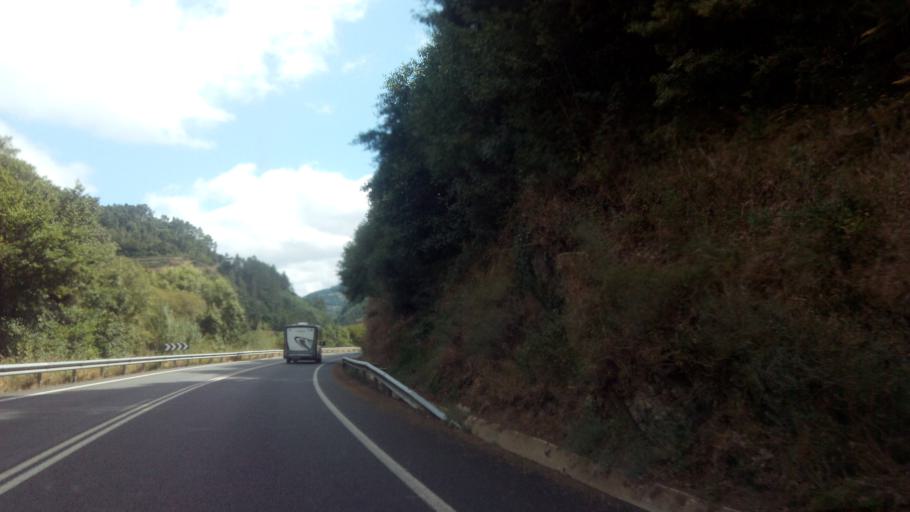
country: ES
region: Galicia
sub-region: Provincia de Ourense
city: Nogueira de Ramuin
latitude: 42.4172
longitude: -7.7770
